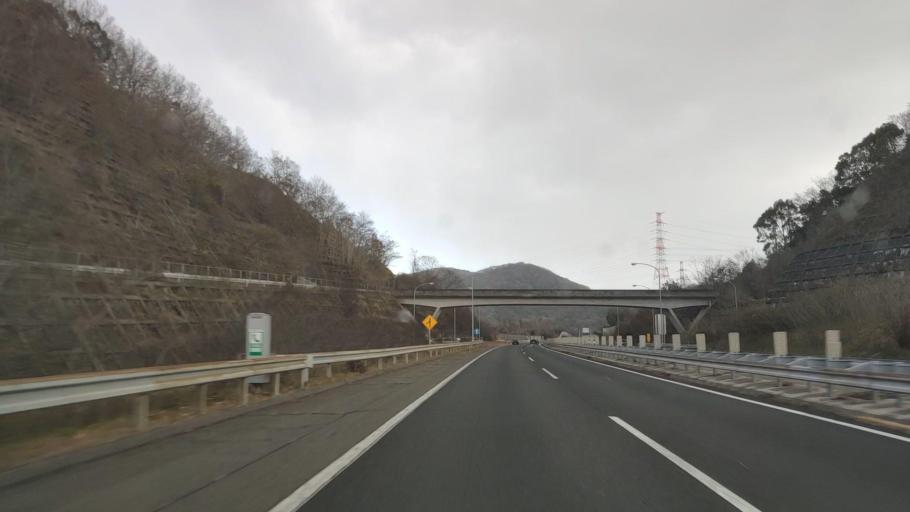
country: JP
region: Okayama
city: Kasaoka
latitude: 34.5357
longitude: 133.5131
